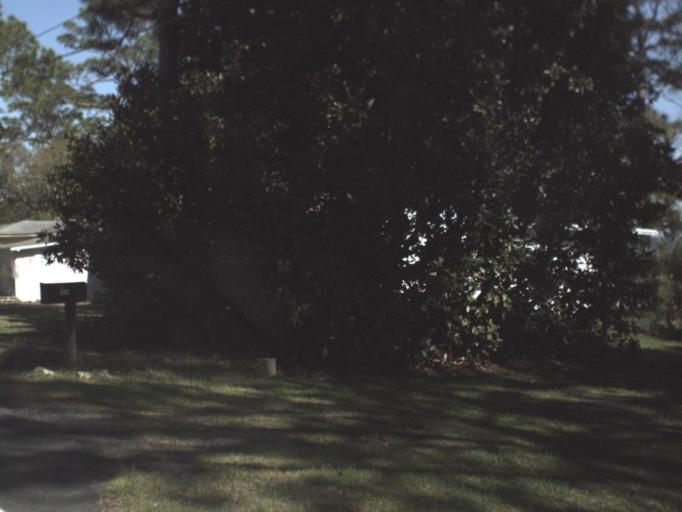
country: US
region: Florida
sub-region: Franklin County
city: Carrabelle
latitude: 29.9031
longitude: -84.5492
